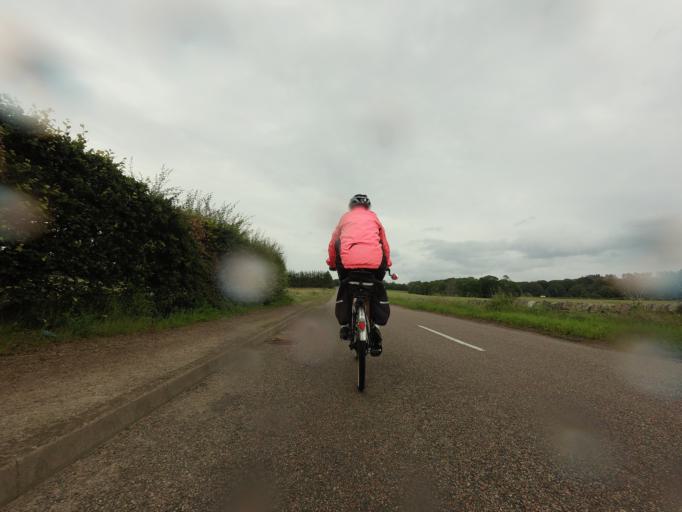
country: GB
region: Scotland
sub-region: Moray
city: Cullen
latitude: 57.6781
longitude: -2.8130
